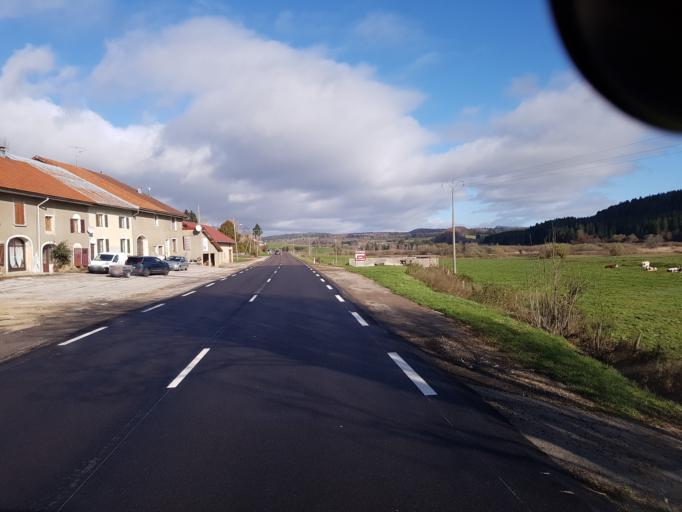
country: FR
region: Franche-Comte
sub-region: Departement du Jura
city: Morbier
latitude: 46.6000
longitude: 5.9607
